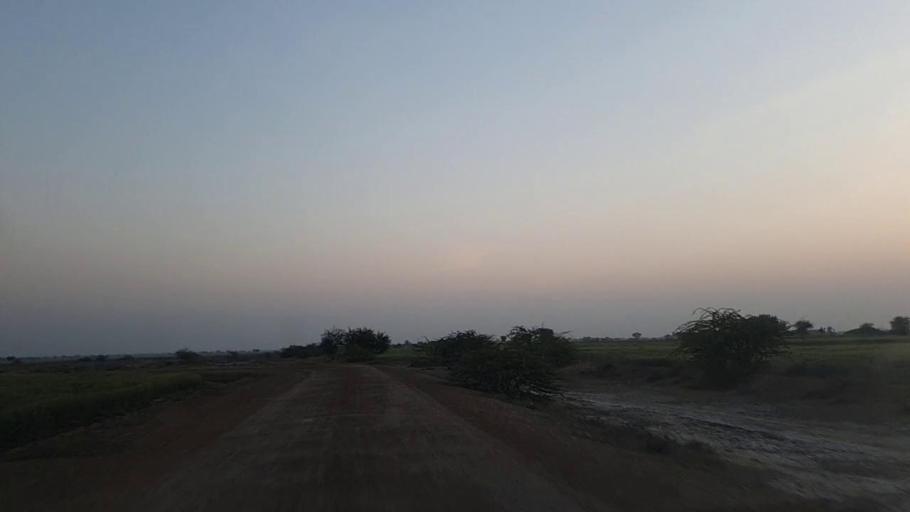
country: PK
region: Sindh
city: Naukot
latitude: 24.9957
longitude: 69.4335
